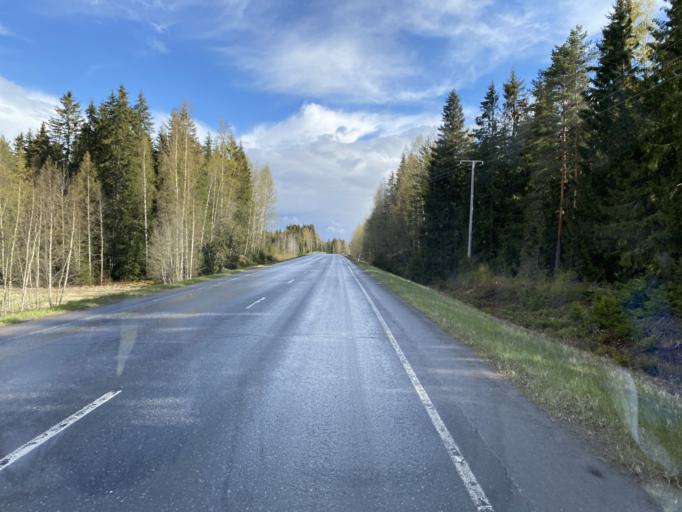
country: FI
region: Pirkanmaa
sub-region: Etelae-Pirkanmaa
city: Viiala
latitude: 61.2385
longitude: 23.7394
